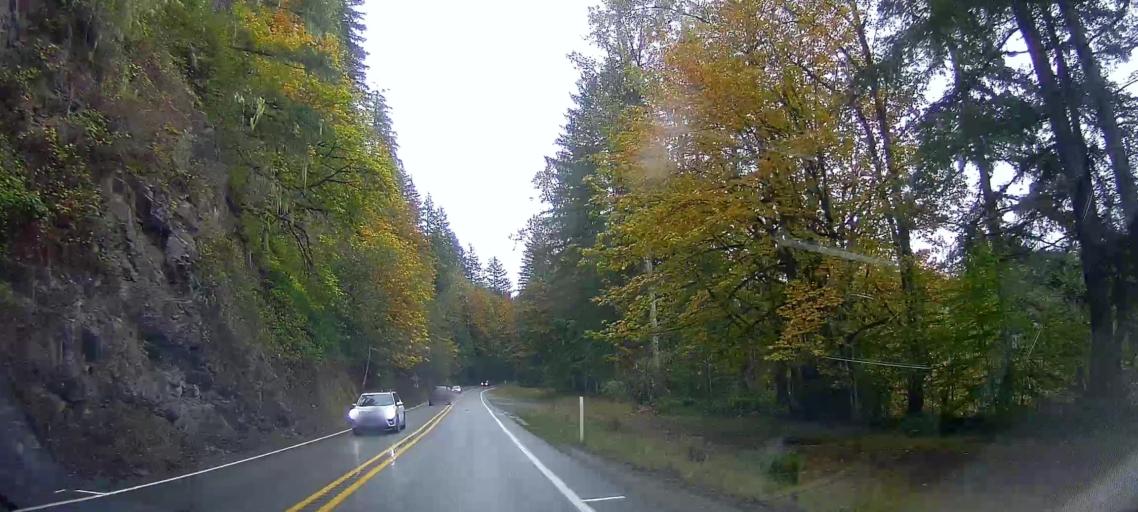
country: US
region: Washington
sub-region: Snohomish County
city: Darrington
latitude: 48.4919
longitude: -121.5654
